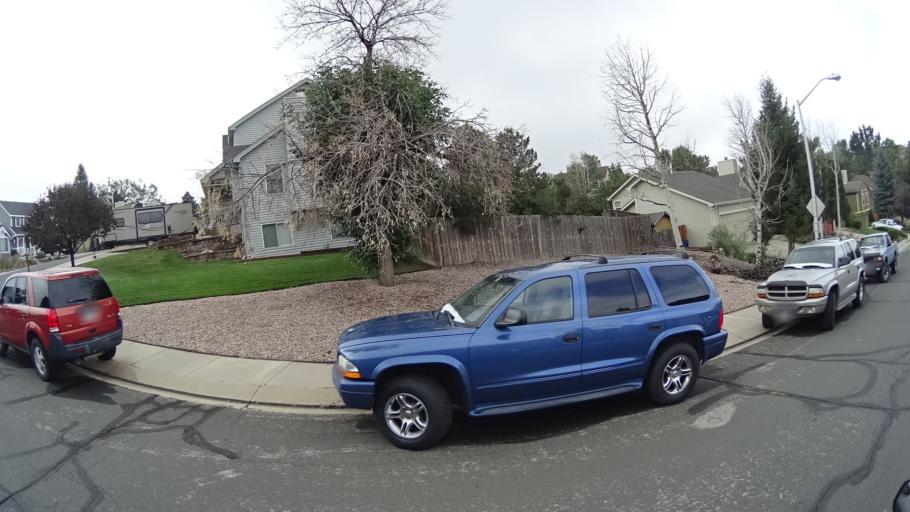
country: US
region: Colorado
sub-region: El Paso County
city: Cimarron Hills
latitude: 38.9243
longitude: -104.7542
